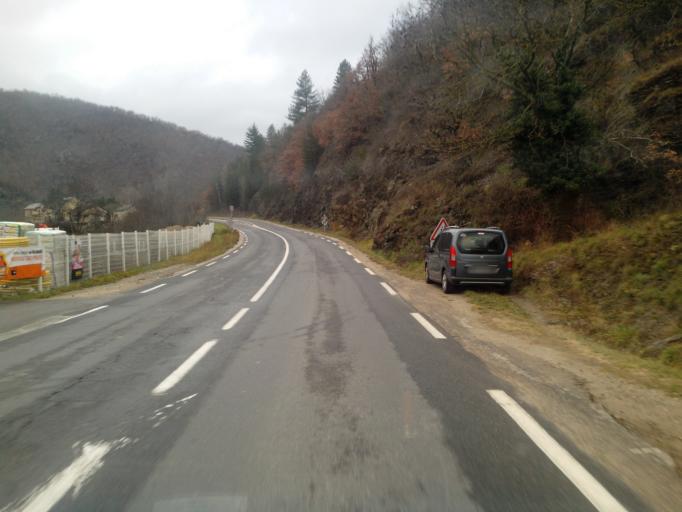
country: FR
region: Languedoc-Roussillon
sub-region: Departement de la Lozere
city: Florac
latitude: 44.3454
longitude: 3.5804
